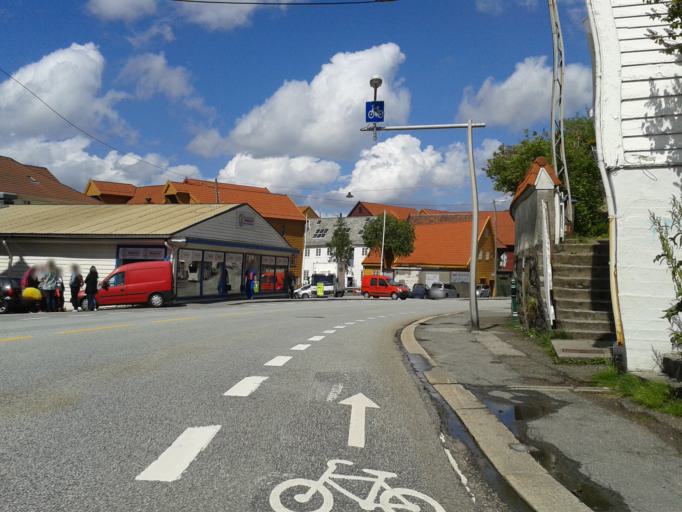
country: NO
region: Hordaland
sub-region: Bergen
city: Bergen
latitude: 60.4070
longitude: 5.3225
